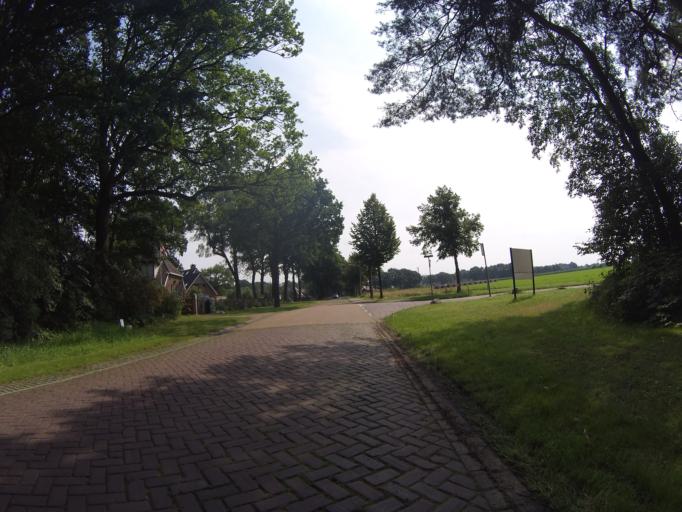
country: NL
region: Drenthe
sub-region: Gemeente Coevorden
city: Sleen
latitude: 52.7910
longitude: 6.7102
